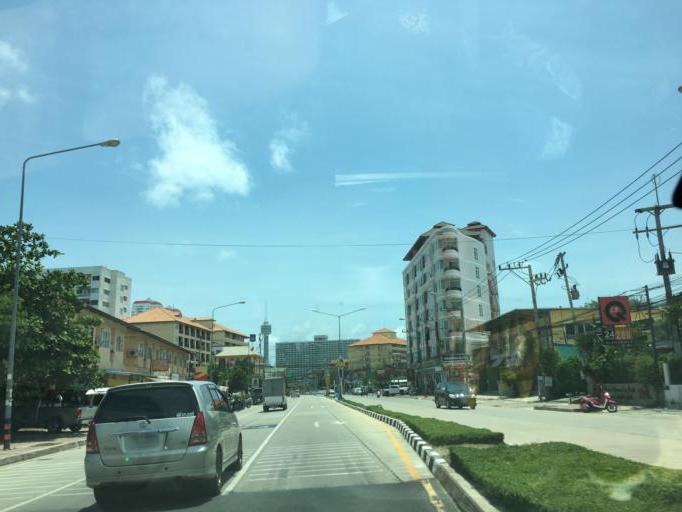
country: TH
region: Chon Buri
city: Phatthaya
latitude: 12.8968
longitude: 100.8741
